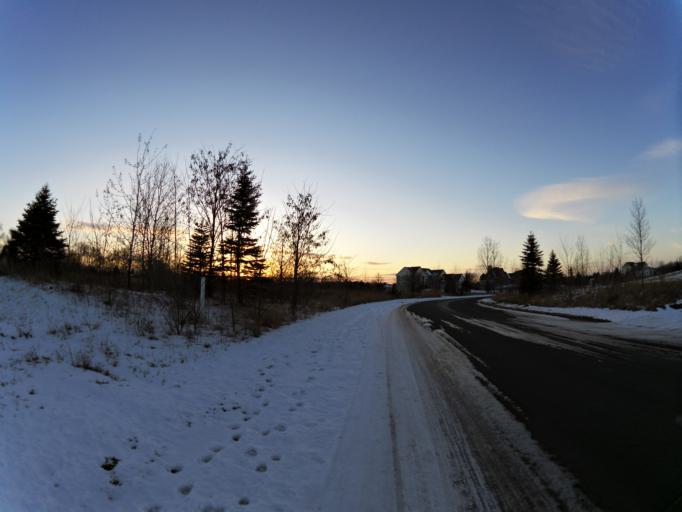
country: US
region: Minnesota
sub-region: Washington County
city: Lake Elmo
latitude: 44.9774
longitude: -92.8499
